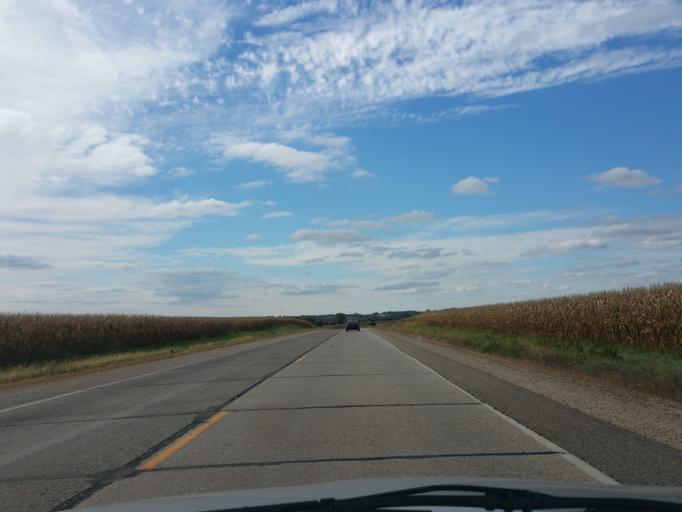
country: US
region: Wisconsin
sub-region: Pierce County
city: Prescott
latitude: 44.7758
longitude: -92.7693
